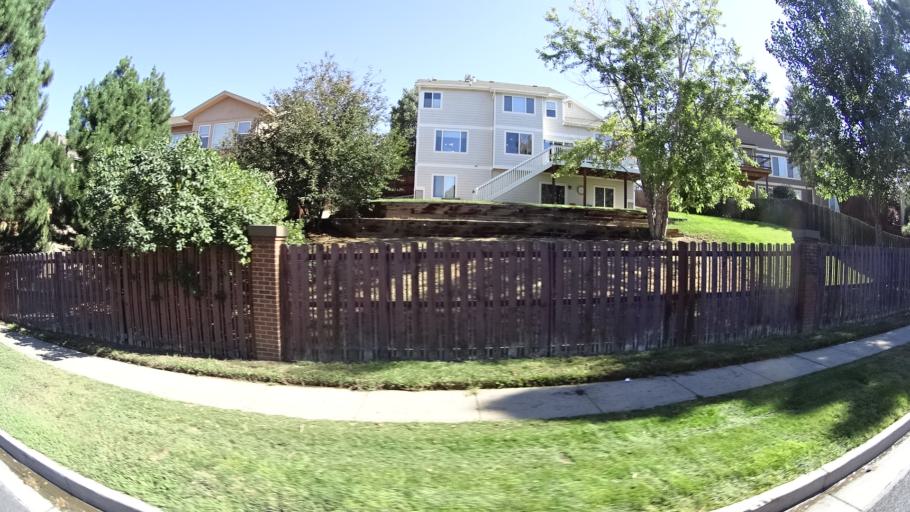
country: US
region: Colorado
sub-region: El Paso County
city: Cimarron Hills
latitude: 38.9219
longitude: -104.7429
